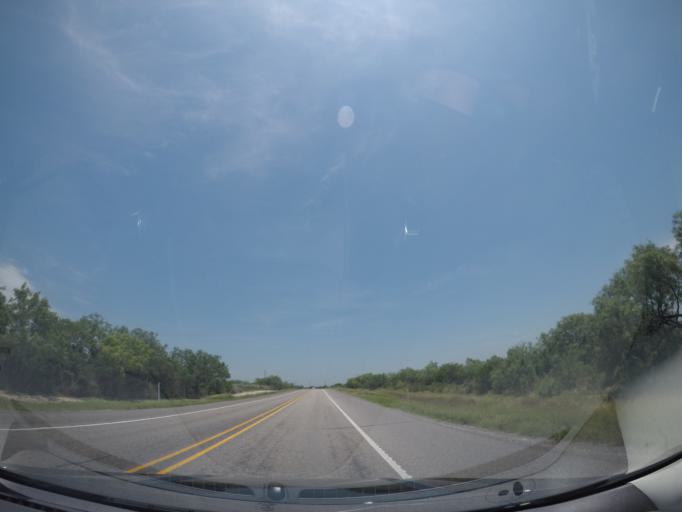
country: US
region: Texas
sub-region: Uvalde County
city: Uvalde Estates
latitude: 29.2029
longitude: -99.8840
